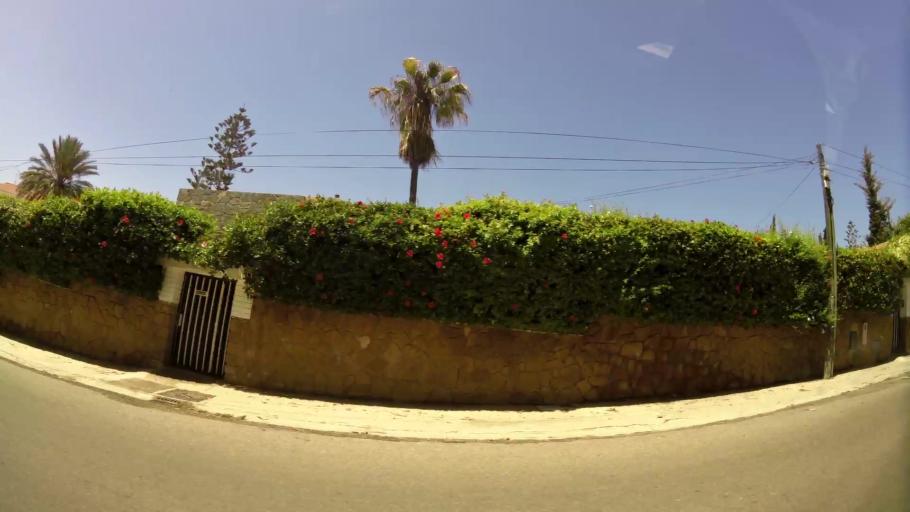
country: MA
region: Souss-Massa-Draa
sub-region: Agadir-Ida-ou-Tnan
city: Agadir
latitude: 30.4291
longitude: -9.5987
